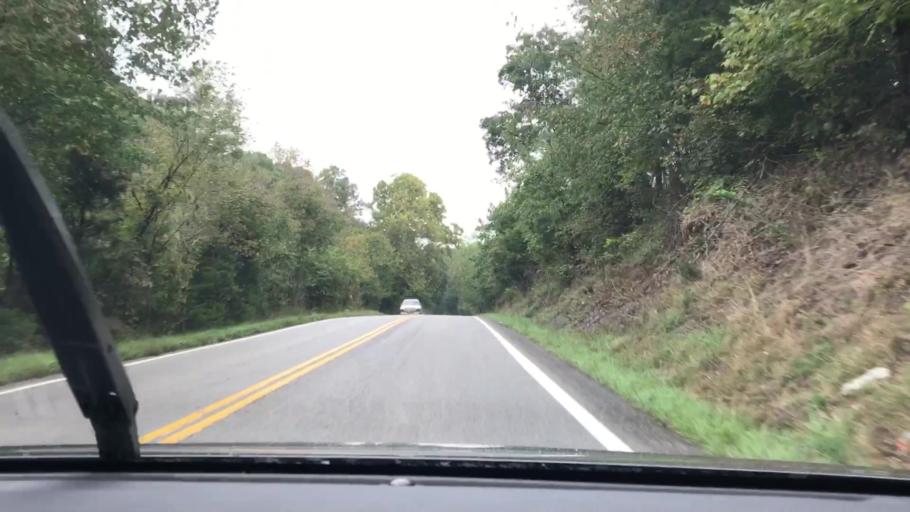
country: US
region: Kentucky
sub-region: Monroe County
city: Tompkinsville
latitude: 36.6499
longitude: -85.7472
